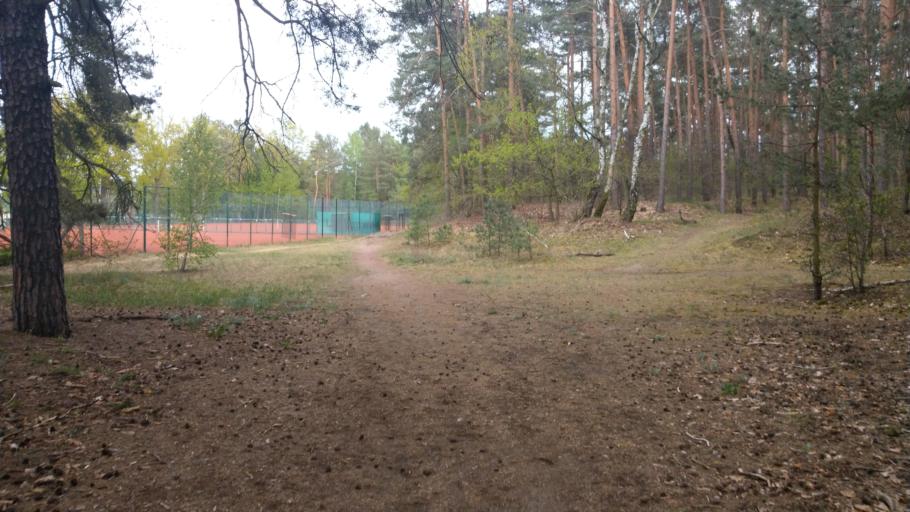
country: DE
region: Brandenburg
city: Luckenwalde
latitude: 52.1032
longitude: 13.1445
